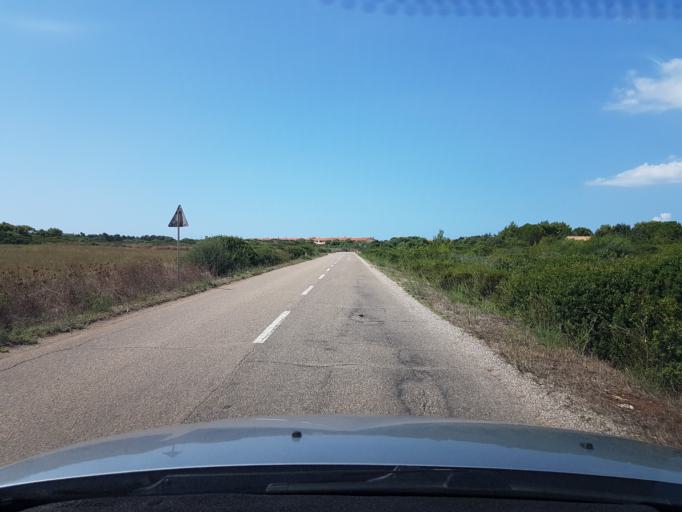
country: IT
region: Sardinia
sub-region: Provincia di Oristano
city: Riola Sardo
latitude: 40.0369
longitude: 8.4197
